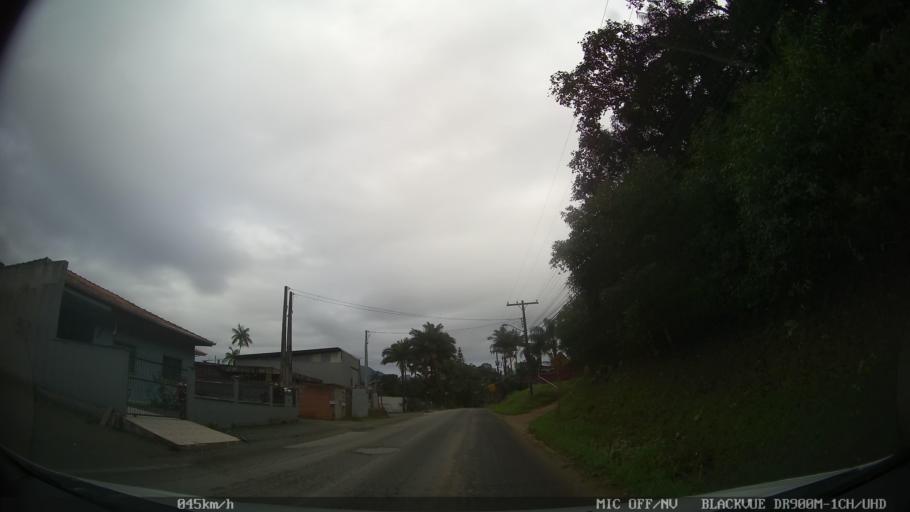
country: BR
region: Santa Catarina
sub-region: Joinville
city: Joinville
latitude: -26.2827
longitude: -48.9248
